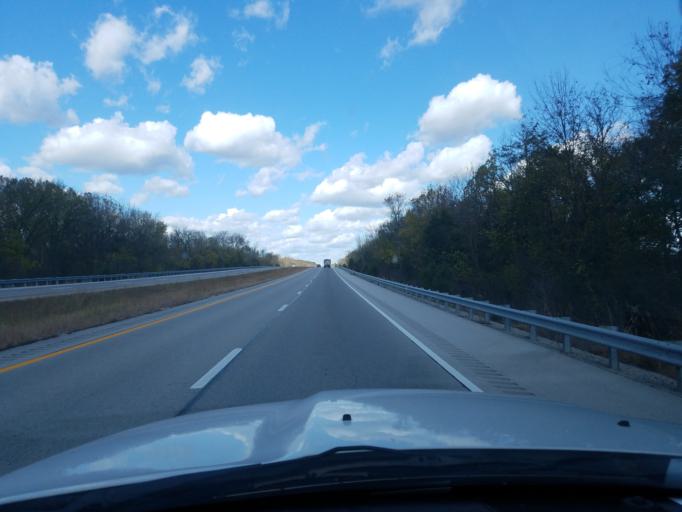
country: US
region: Kentucky
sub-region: Butler County
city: Morgantown
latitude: 37.1327
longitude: -86.6477
